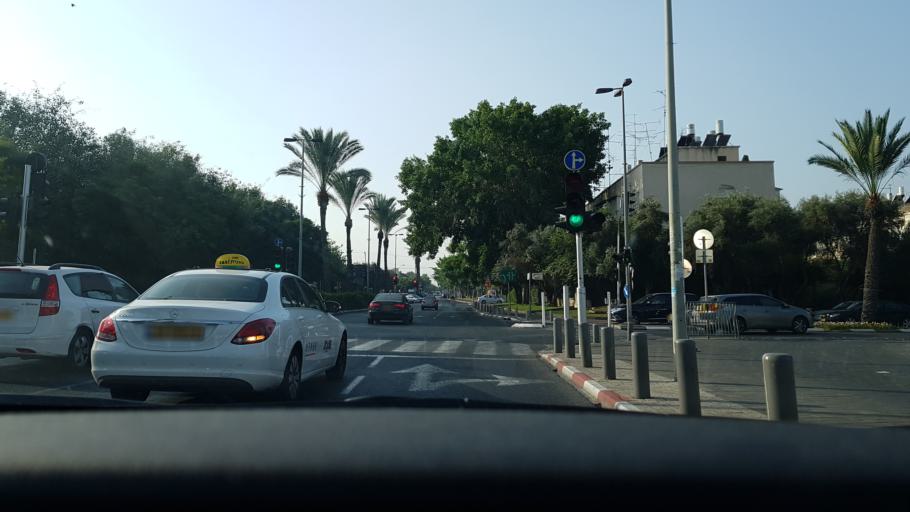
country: IL
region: Tel Aviv
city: Tel Aviv
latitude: 32.0603
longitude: 34.7919
